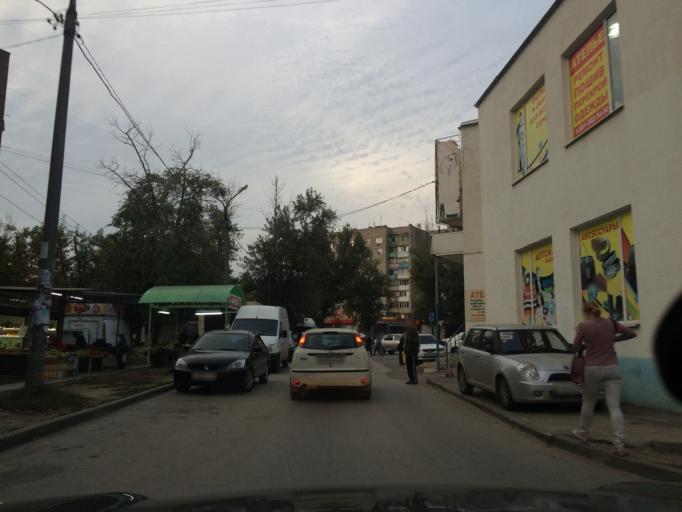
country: RU
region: Rostov
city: Rostov-na-Donu
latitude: 47.2026
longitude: 39.6167
